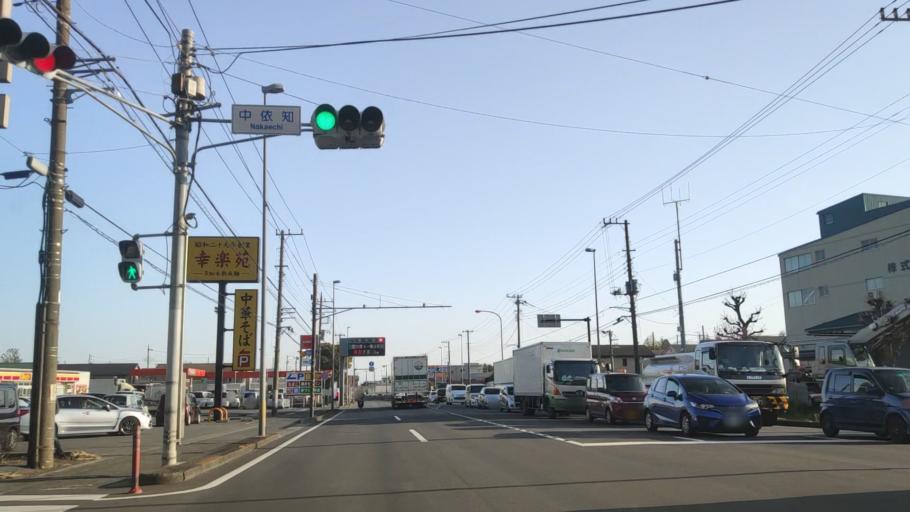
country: JP
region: Kanagawa
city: Zama
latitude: 35.4792
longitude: 139.3662
